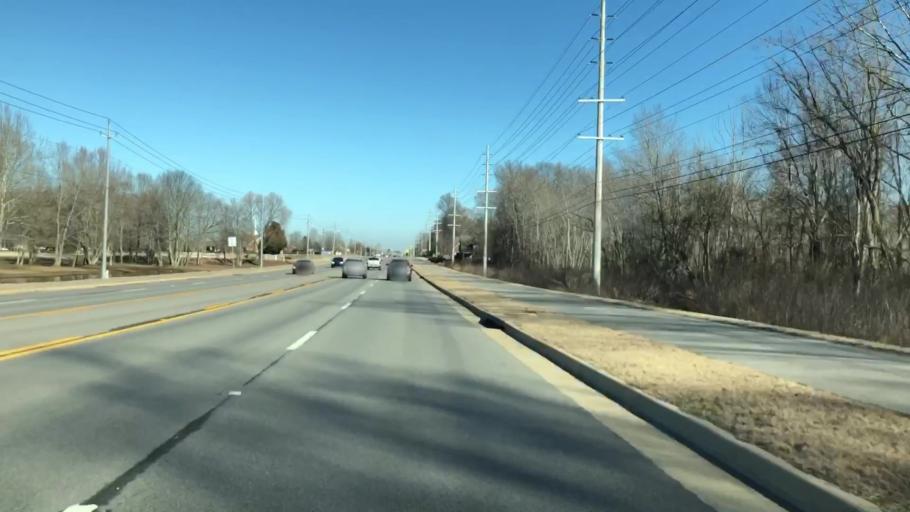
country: US
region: Alabama
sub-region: Madison County
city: Madison
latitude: 34.7146
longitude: -86.7864
